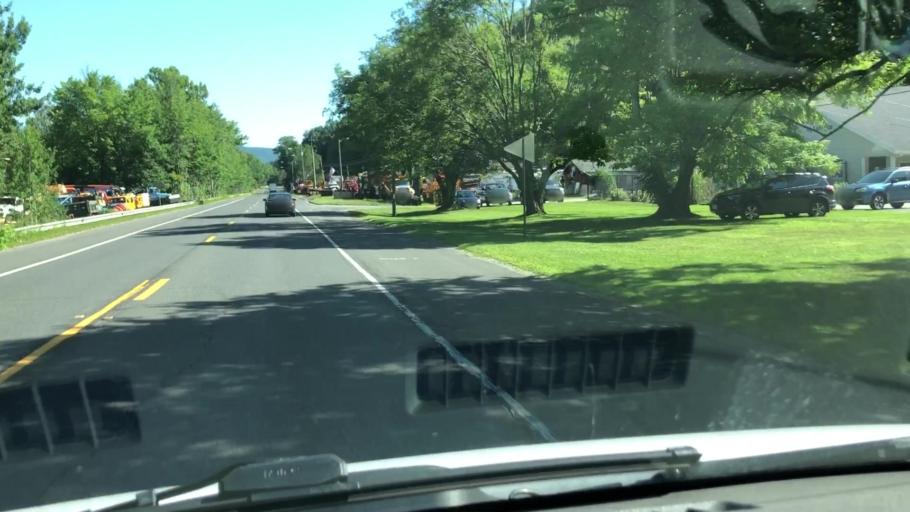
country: US
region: Massachusetts
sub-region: Berkshire County
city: Lanesborough
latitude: 42.5007
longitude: -73.1961
